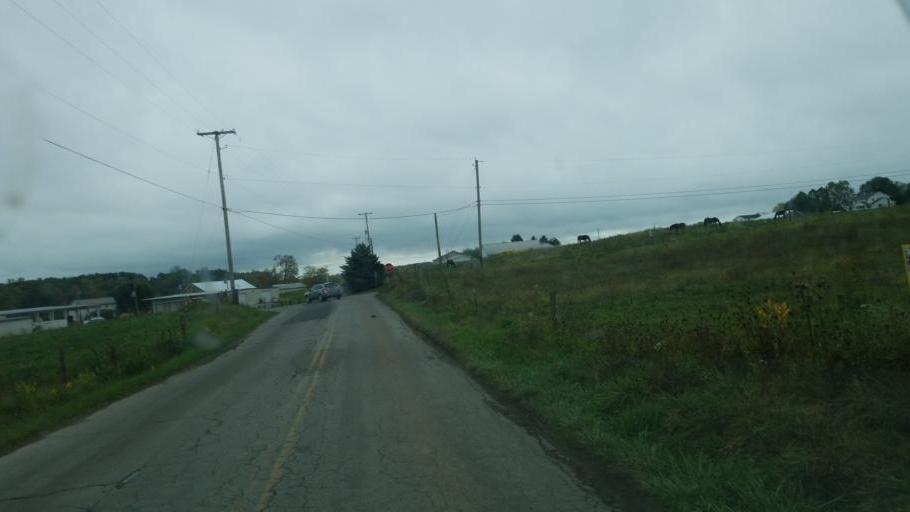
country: US
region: Ohio
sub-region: Holmes County
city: Millersburg
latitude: 40.6246
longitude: -81.8131
